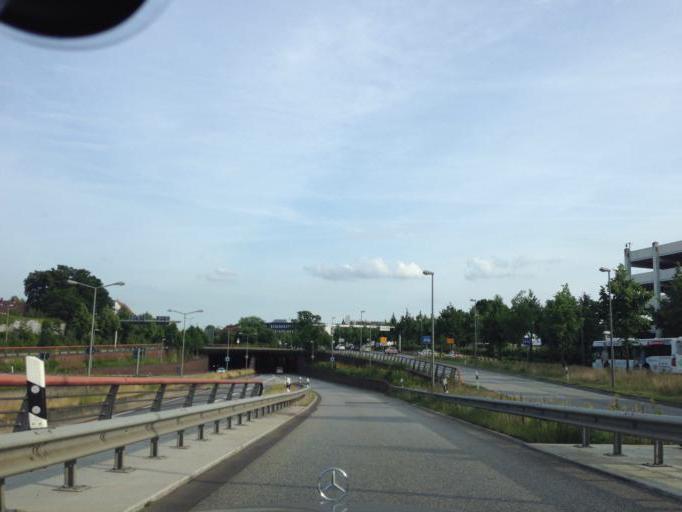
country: DE
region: Hamburg
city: Fuhlsbuettel
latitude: 53.6264
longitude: 10.0088
